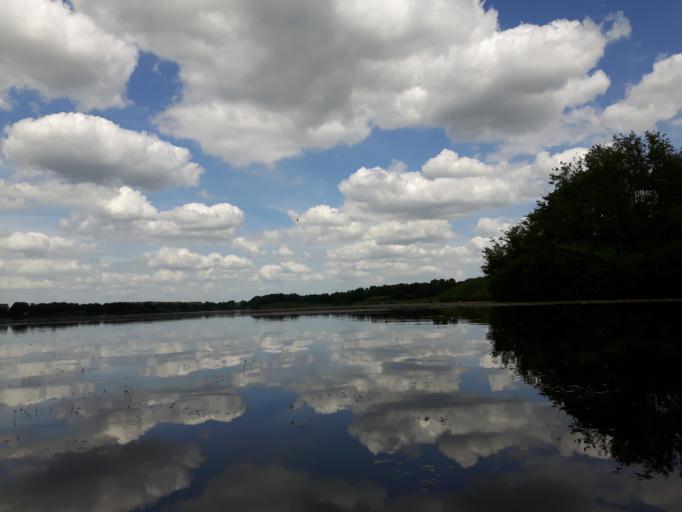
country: DE
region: Schleswig-Holstein
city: Muhbrook
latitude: 54.1415
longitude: 10.0079
